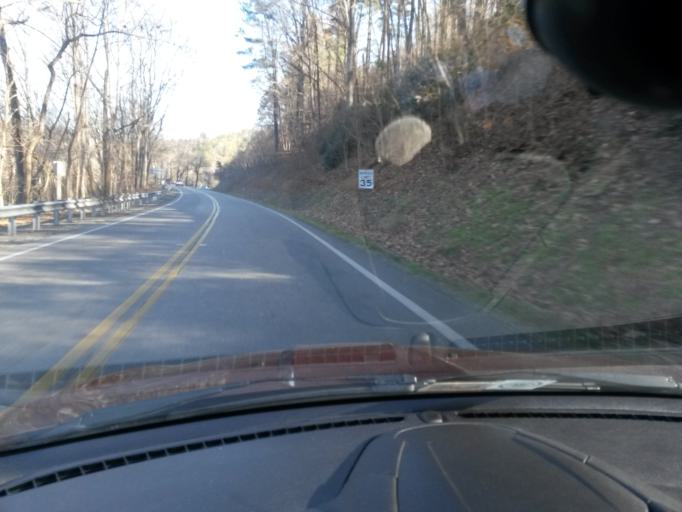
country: US
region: Virginia
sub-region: Henry County
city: Bassett
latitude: 36.7642
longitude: -80.0028
